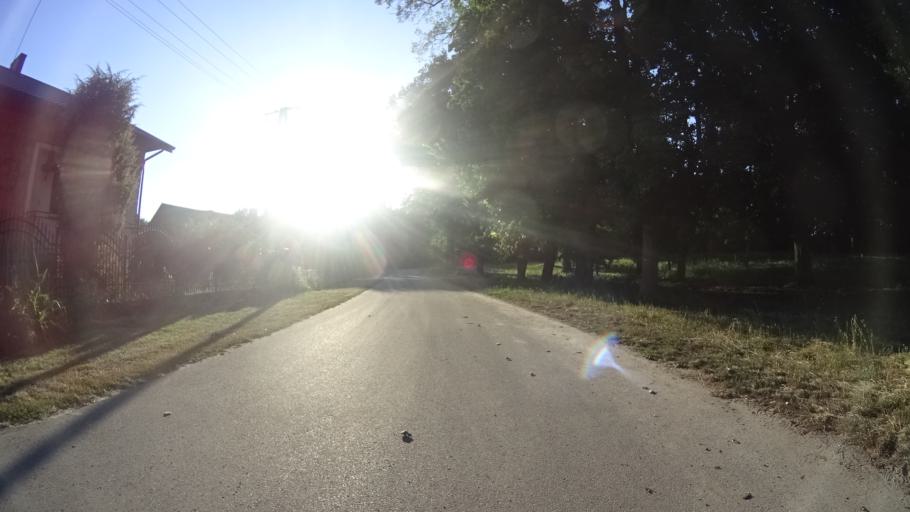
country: PL
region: Masovian Voivodeship
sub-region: Powiat bialobrzeski
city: Wysmierzyce
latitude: 51.6573
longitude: 20.7787
